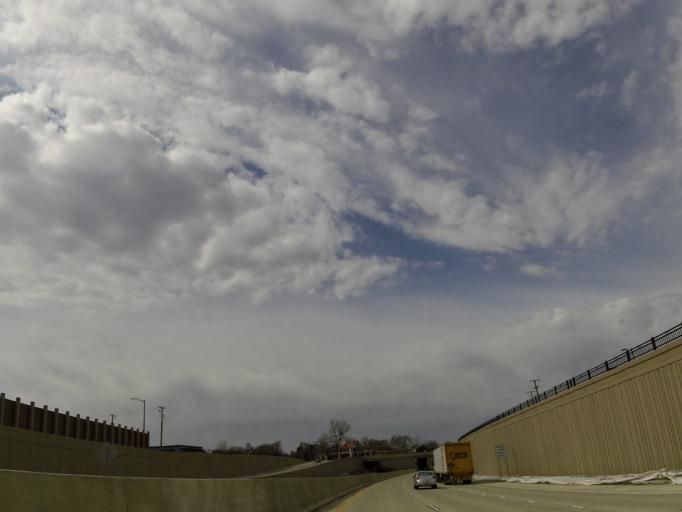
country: US
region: Minnesota
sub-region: Dakota County
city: Burnsville
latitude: 44.7729
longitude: -93.3018
